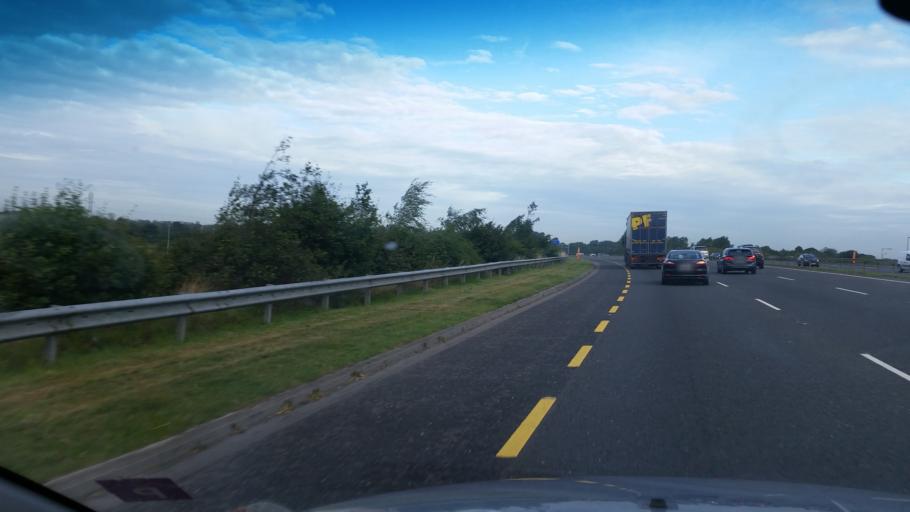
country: IE
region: Leinster
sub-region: Dublin City
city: Finglas
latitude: 53.4187
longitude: -6.3209
